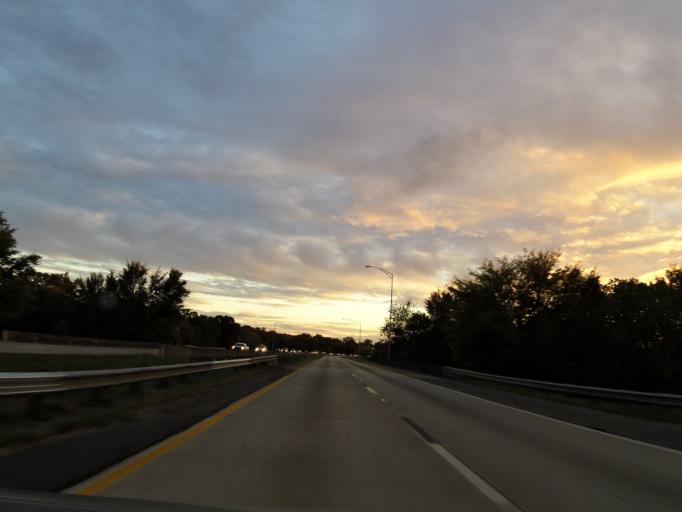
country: US
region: Alabama
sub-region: Jefferson County
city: Irondale
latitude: 33.5740
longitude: -86.7172
